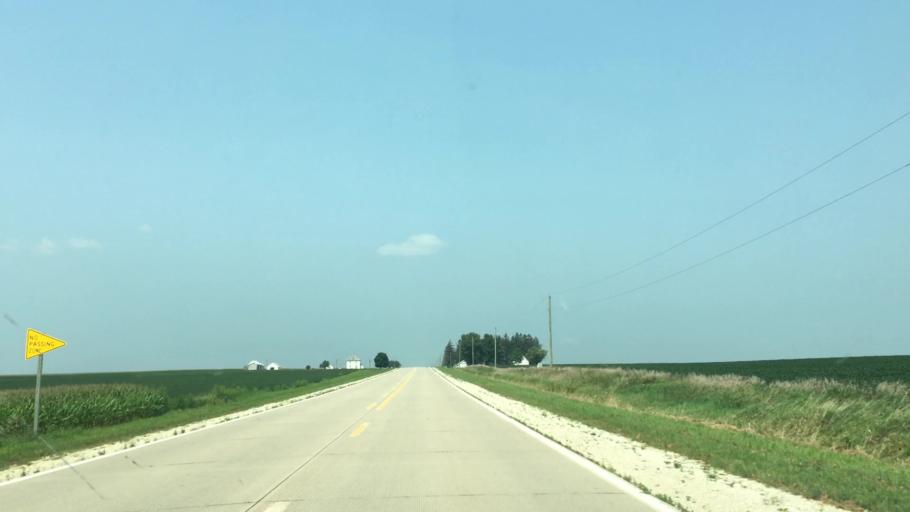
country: US
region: Iowa
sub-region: Fayette County
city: Oelwein
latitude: 42.7061
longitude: -91.8048
